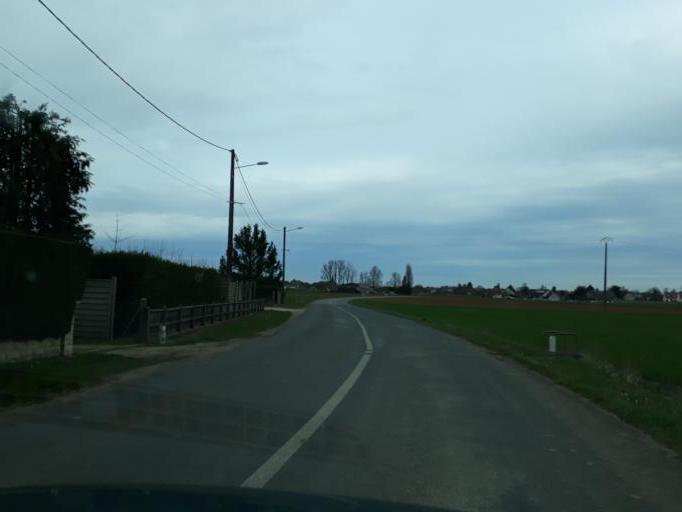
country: FR
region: Centre
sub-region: Departement du Loir-et-Cher
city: Villebarou
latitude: 47.6419
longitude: 1.2983
